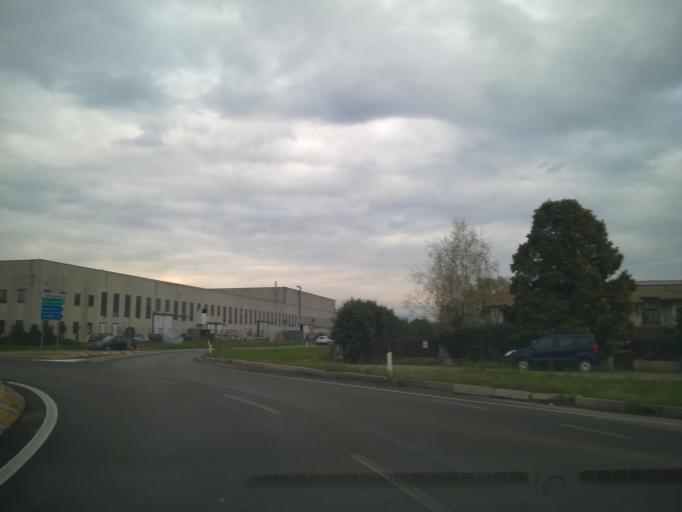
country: IT
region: Veneto
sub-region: Provincia di Vicenza
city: Marano Vicentino
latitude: 45.6759
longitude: 11.4577
